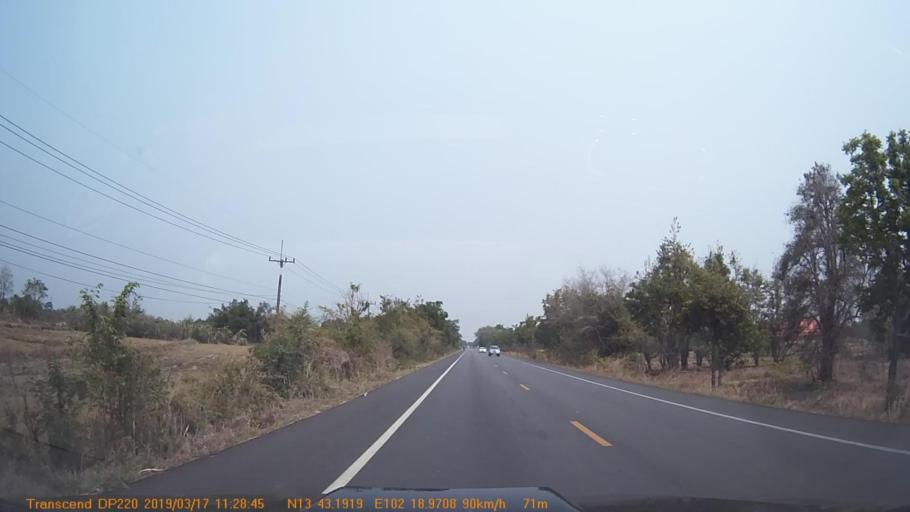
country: TH
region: Sa Kaeo
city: Watthana Nakhon
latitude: 13.7202
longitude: 102.3162
